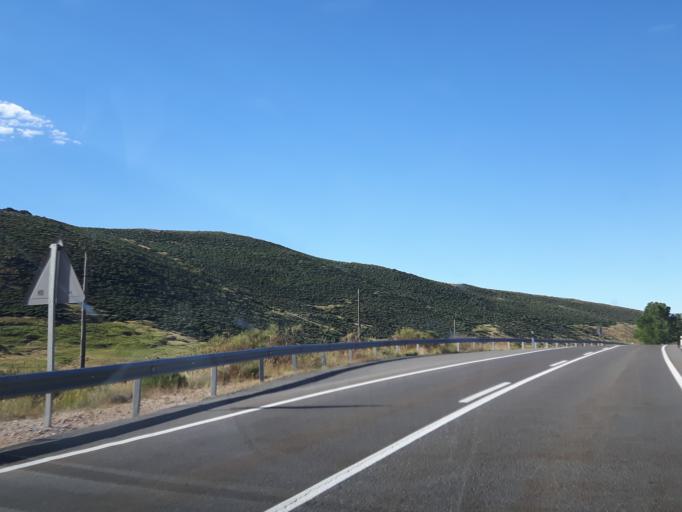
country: ES
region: Castille and Leon
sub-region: Provincia de Avila
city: Mengamunoz
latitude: 40.4722
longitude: -5.0159
